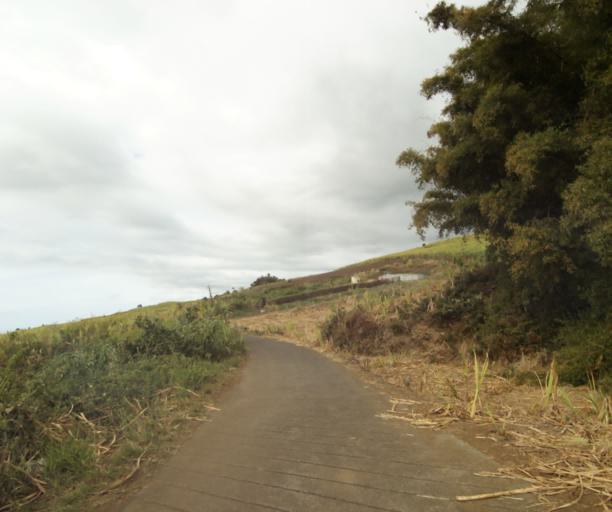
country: RE
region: Reunion
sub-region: Reunion
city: Saint-Paul
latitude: -21.0279
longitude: 55.3189
